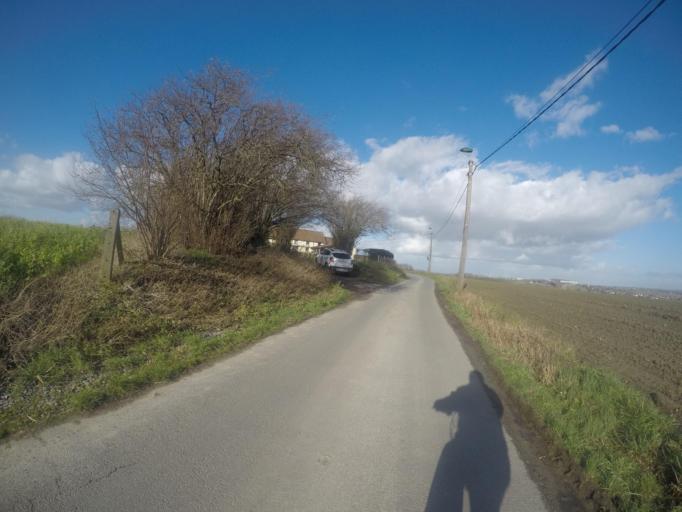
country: BE
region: Wallonia
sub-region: Province du Brabant Wallon
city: Rebecq-Rognon
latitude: 50.6824
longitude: 4.1480
